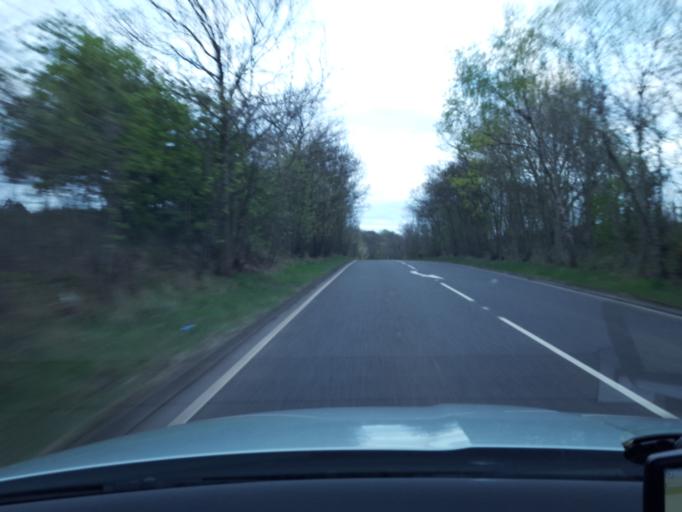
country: GB
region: Scotland
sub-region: West Lothian
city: Bathgate
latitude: 55.9496
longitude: -3.6638
